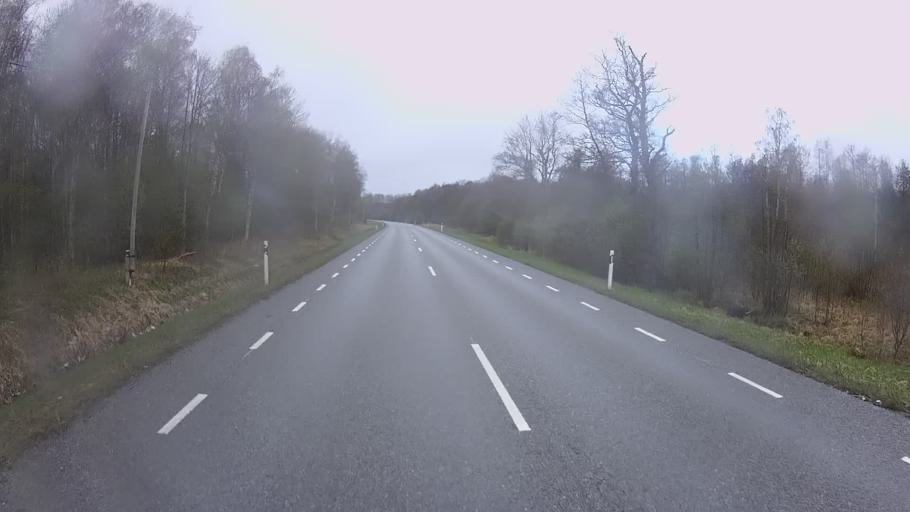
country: EE
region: Hiiumaa
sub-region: Kaerdla linn
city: Kardla
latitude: 59.0033
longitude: 22.5747
